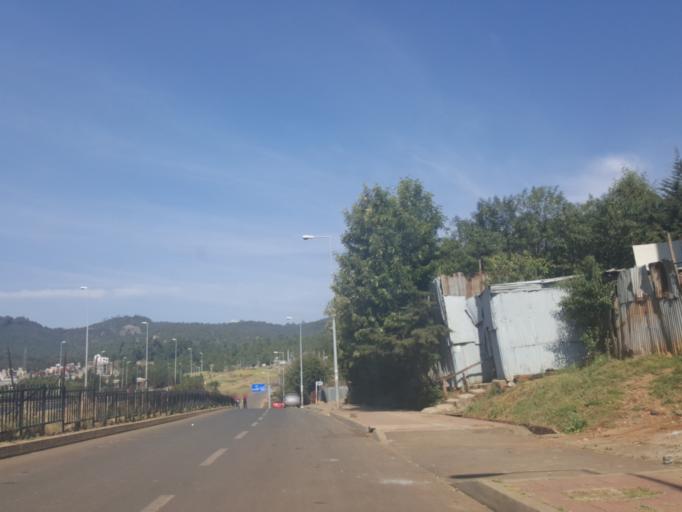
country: ET
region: Adis Abeba
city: Addis Ababa
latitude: 9.0676
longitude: 38.7253
